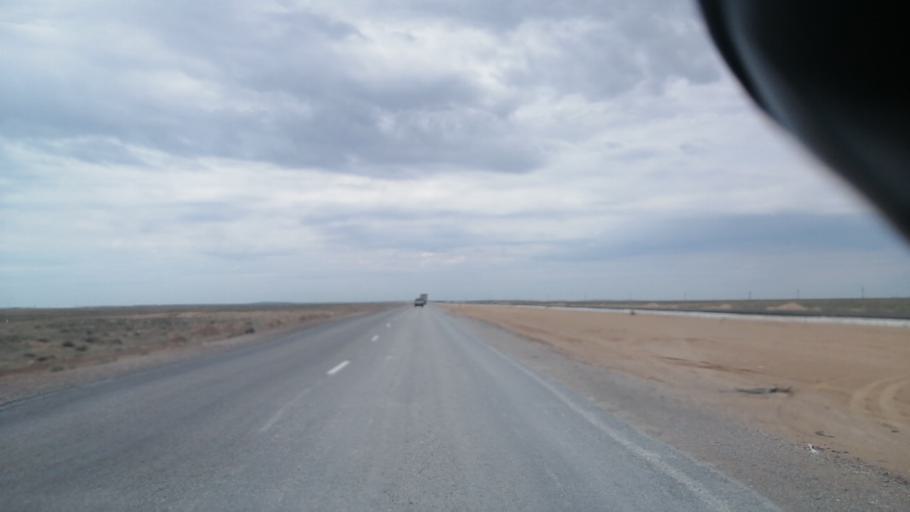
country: KZ
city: Priozersk
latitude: 46.5372
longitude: 74.1551
